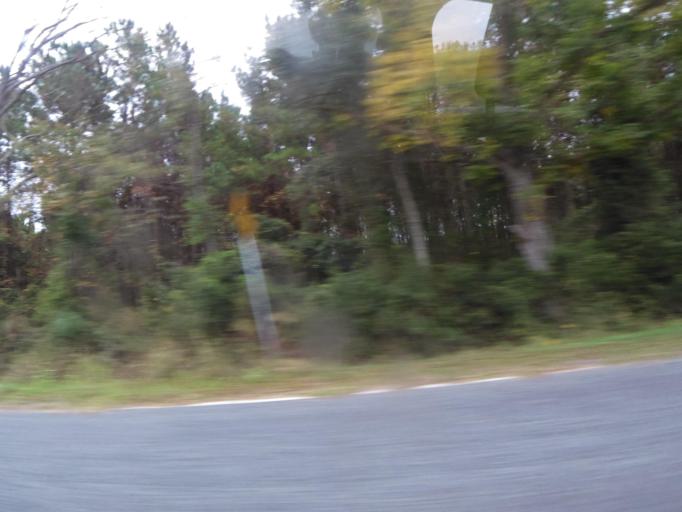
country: US
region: Georgia
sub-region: Charlton County
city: Folkston
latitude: 30.9015
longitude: -82.0733
